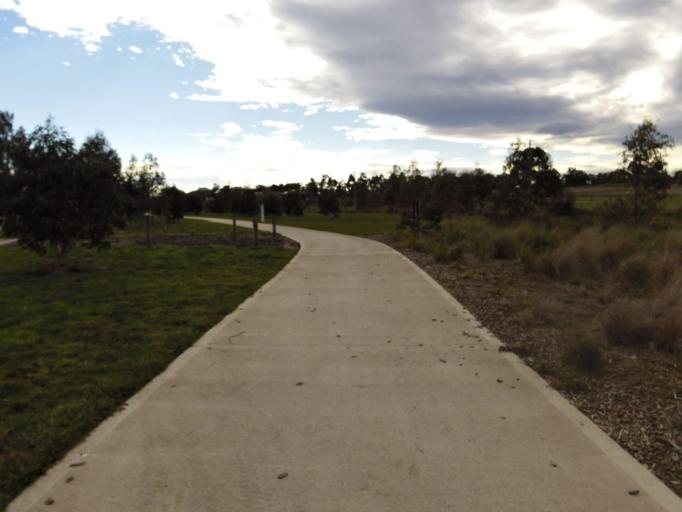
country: AU
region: Victoria
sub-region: Whittlesea
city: Epping
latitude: -37.6179
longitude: 145.0426
